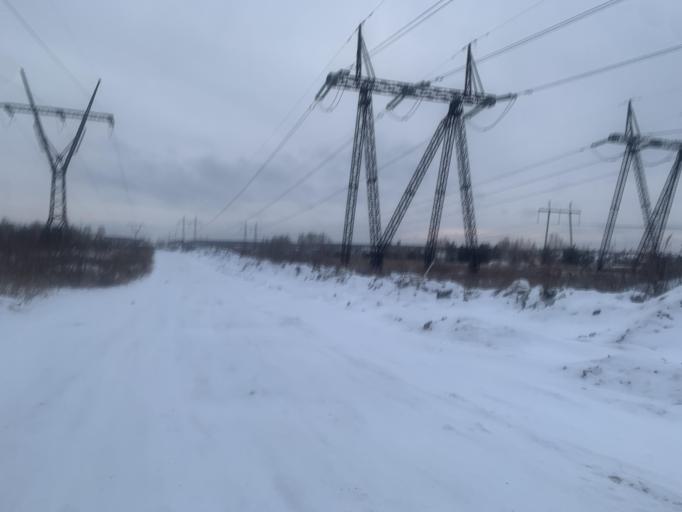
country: RU
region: Chelyabinsk
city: Roshchino
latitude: 55.1924
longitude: 61.2595
